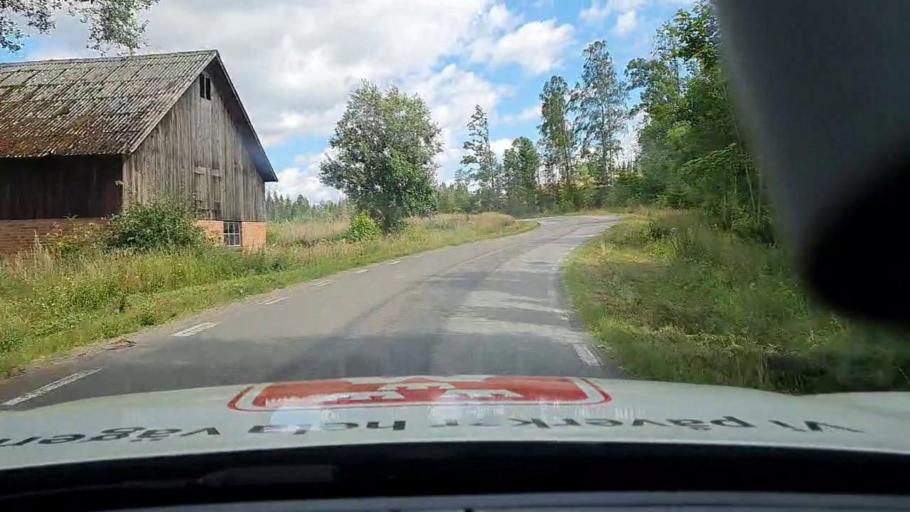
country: SE
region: Vaestra Goetaland
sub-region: Karlsborgs Kommun
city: Molltorp
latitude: 58.6045
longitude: 14.2852
